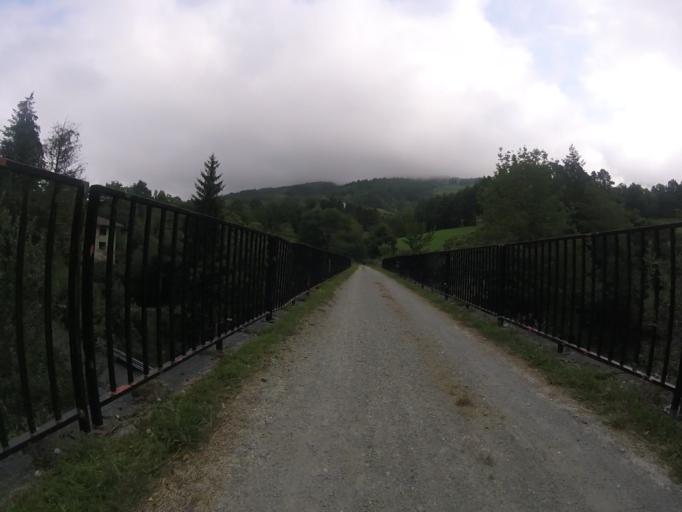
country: ES
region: Navarre
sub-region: Provincia de Navarra
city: Leitza
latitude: 43.0852
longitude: -1.9022
